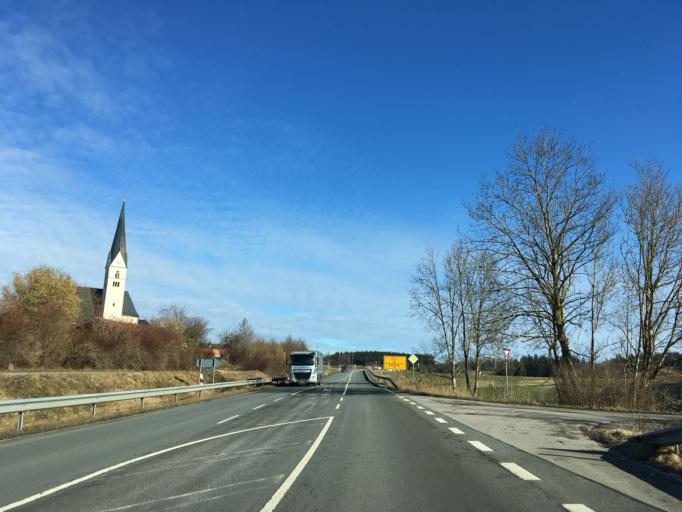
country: DE
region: Bavaria
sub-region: Upper Bavaria
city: Babensham
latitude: 48.0803
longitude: 12.2708
